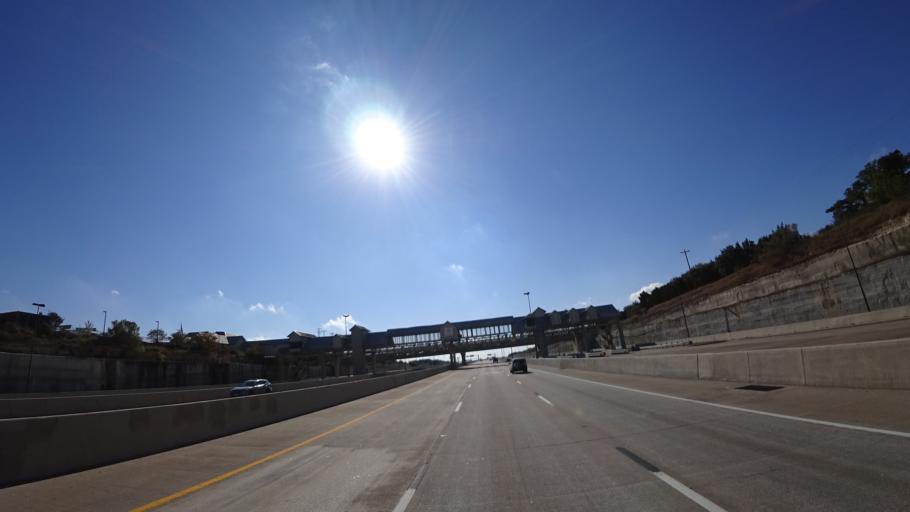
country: US
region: Texas
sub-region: Williamson County
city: Cedar Park
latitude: 30.5151
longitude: -97.8136
